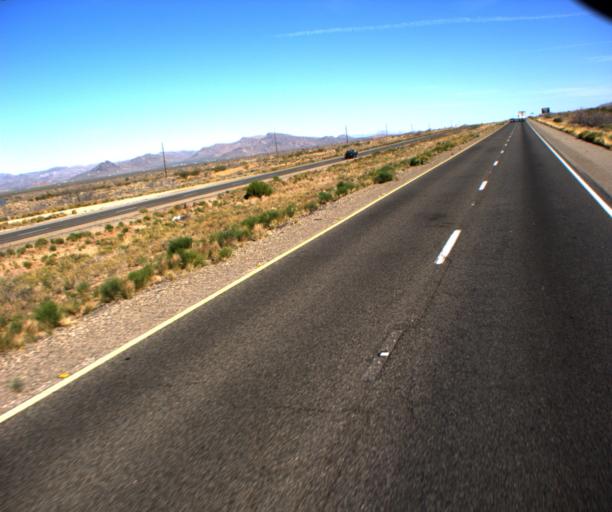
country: US
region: Arizona
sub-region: Mohave County
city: Golden Valley
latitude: 35.2839
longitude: -114.1773
